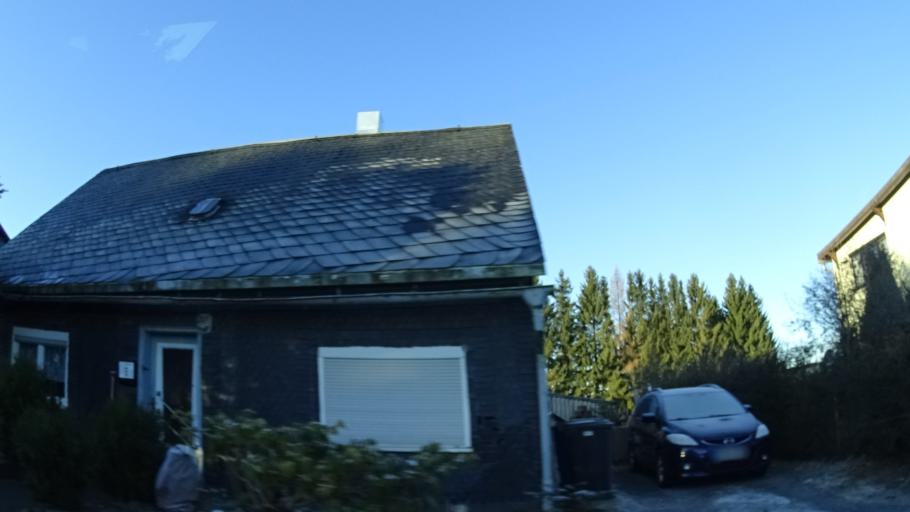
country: DE
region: Thuringia
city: Judenbach
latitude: 50.4066
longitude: 11.2286
